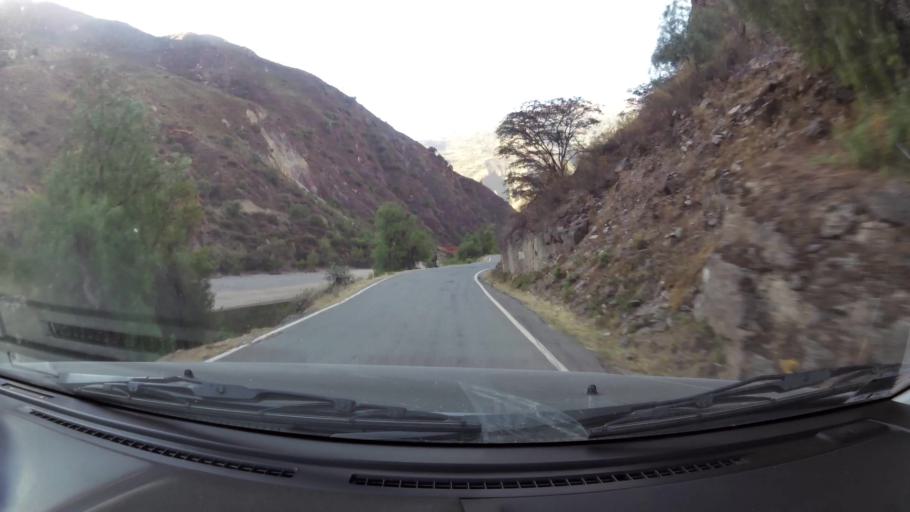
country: PE
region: Huancavelica
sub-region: Provincia de Churcampa
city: La Esmeralda
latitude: -12.5820
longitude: -74.6946
